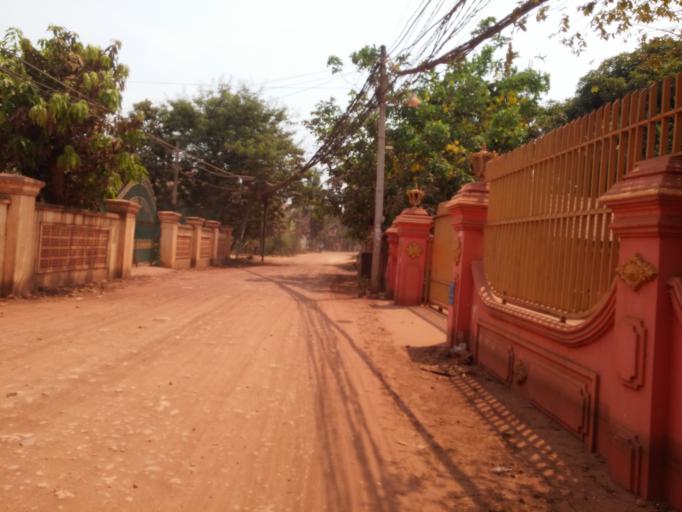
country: KH
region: Siem Reap
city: Siem Reap
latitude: 13.3716
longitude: 103.8479
